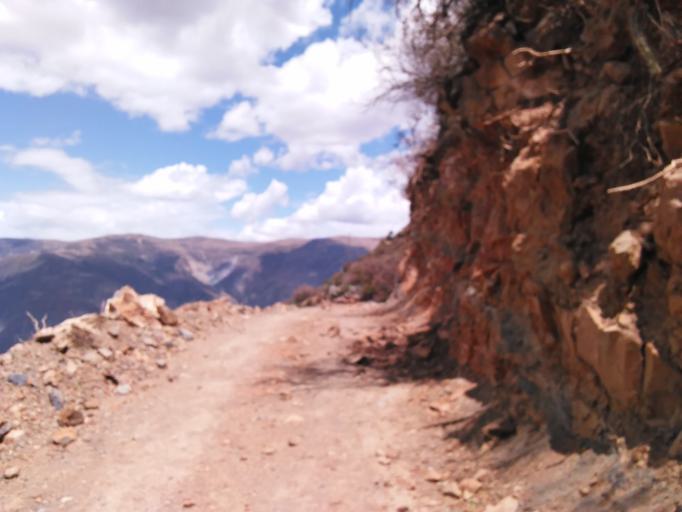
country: PE
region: Ayacucho
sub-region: Provincia de Victor Fajardo
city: Canaria
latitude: -13.8826
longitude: -73.9380
